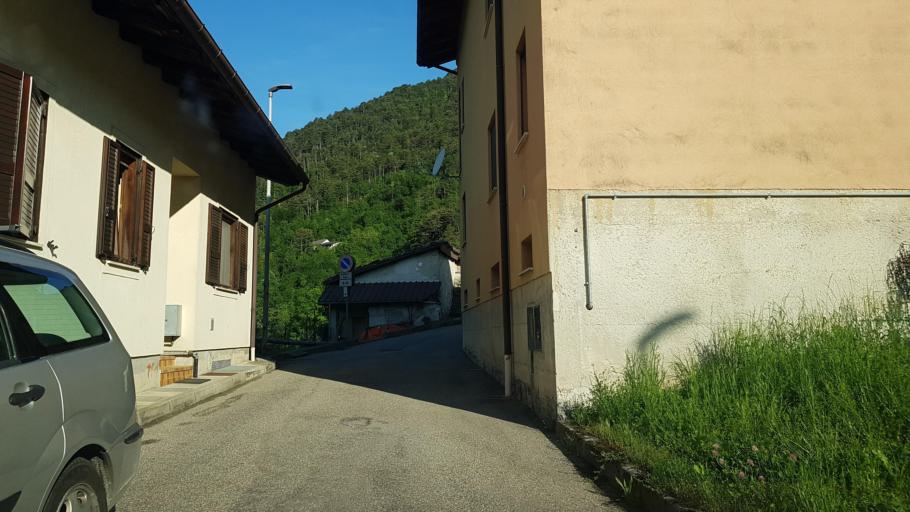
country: IT
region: Friuli Venezia Giulia
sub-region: Provincia di Udine
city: Moggio di Sotto
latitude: 46.4102
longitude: 13.1866
